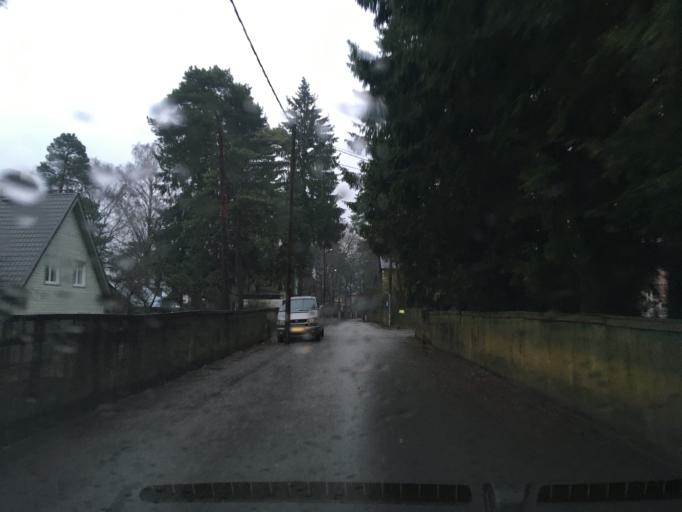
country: EE
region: Harju
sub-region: Tallinna linn
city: Tallinn
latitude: 59.3887
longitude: 24.6940
